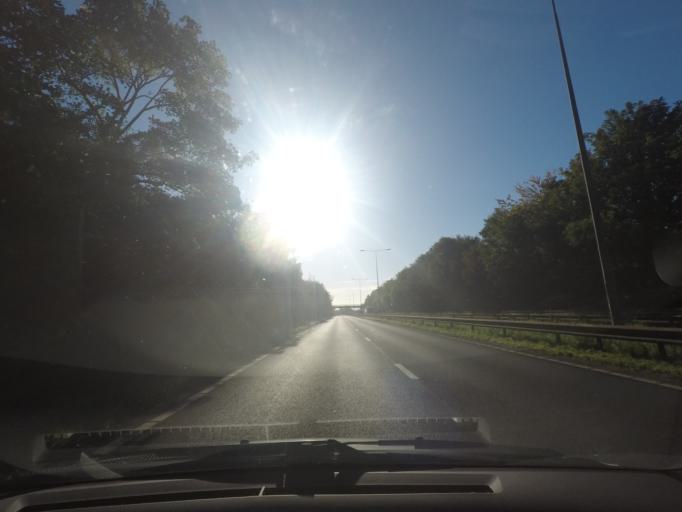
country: GB
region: England
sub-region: East Riding of Yorkshire
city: Brough
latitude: 53.7417
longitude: -0.5653
